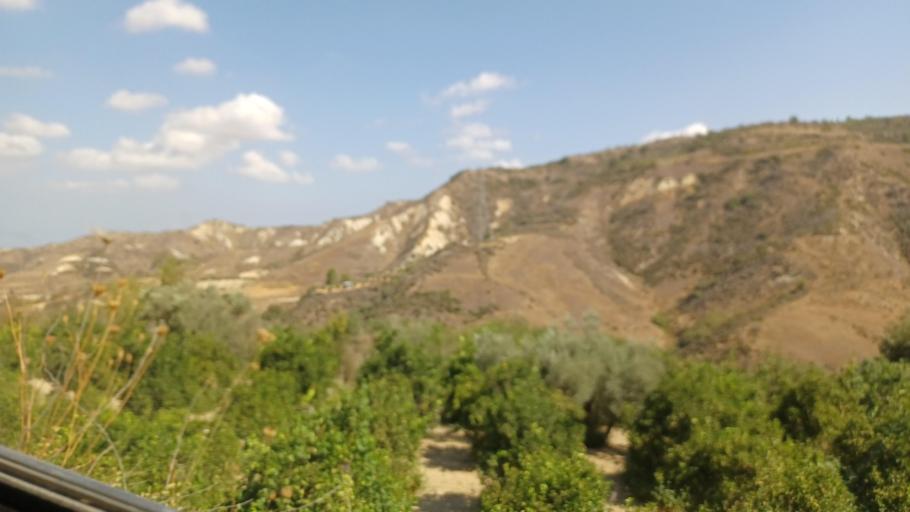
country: CY
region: Pafos
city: Tala
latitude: 34.9364
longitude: 32.4787
